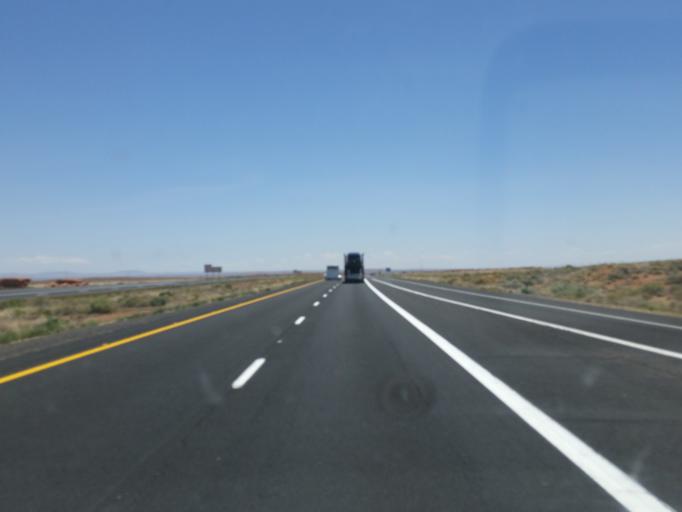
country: US
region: Arizona
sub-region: Coconino County
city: LeChee
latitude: 35.1097
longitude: -111.0271
